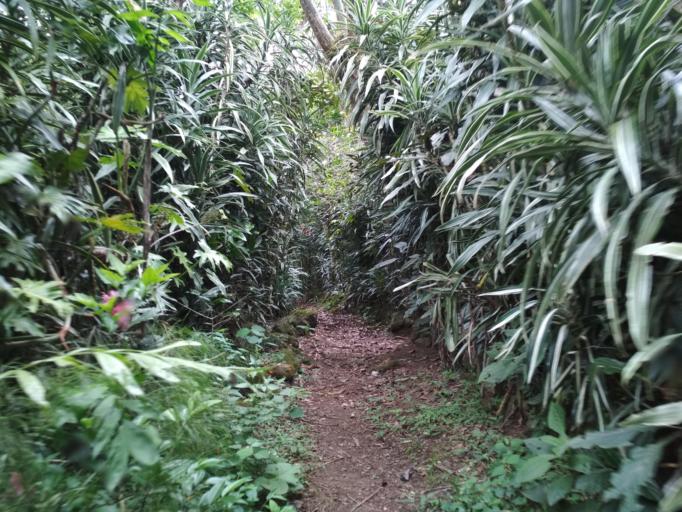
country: MX
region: Veracruz
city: Jilotepec
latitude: 19.6187
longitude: -96.9297
